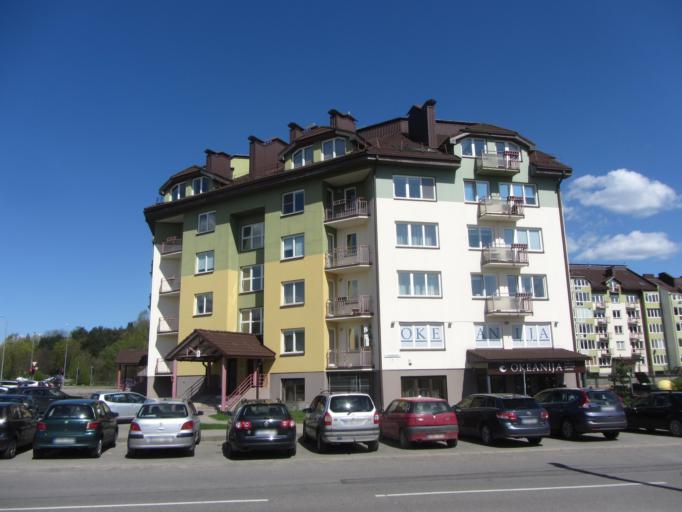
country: LT
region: Vilnius County
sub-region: Vilnius
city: Fabijoniskes
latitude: 54.7520
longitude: 25.2704
